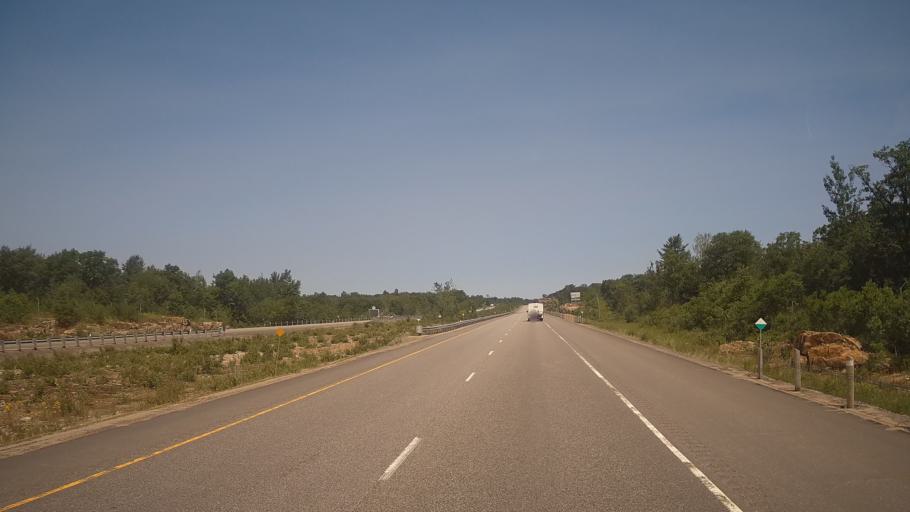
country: CA
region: Ontario
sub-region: Parry Sound District
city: Parry Sound
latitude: 45.1263
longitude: -79.7907
